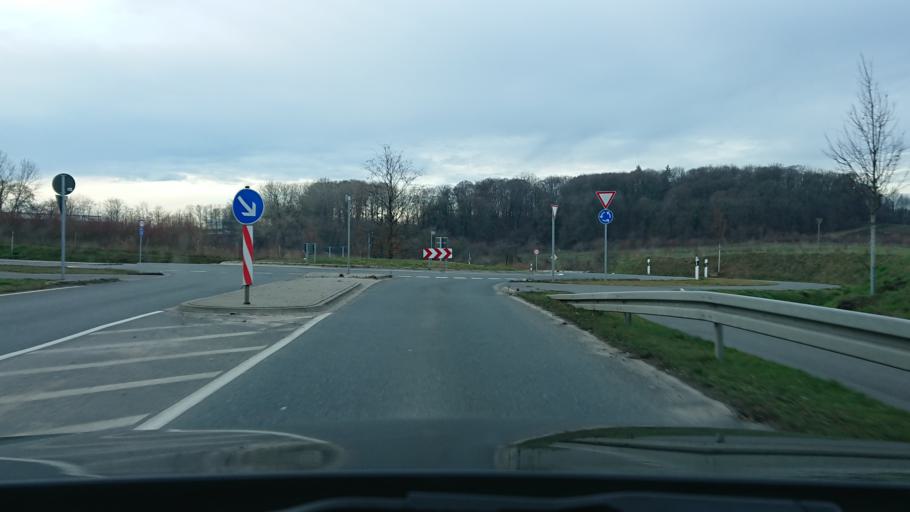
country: DE
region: North Rhine-Westphalia
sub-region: Regierungsbezirk Koln
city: Frechen
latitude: 50.9213
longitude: 6.7956
